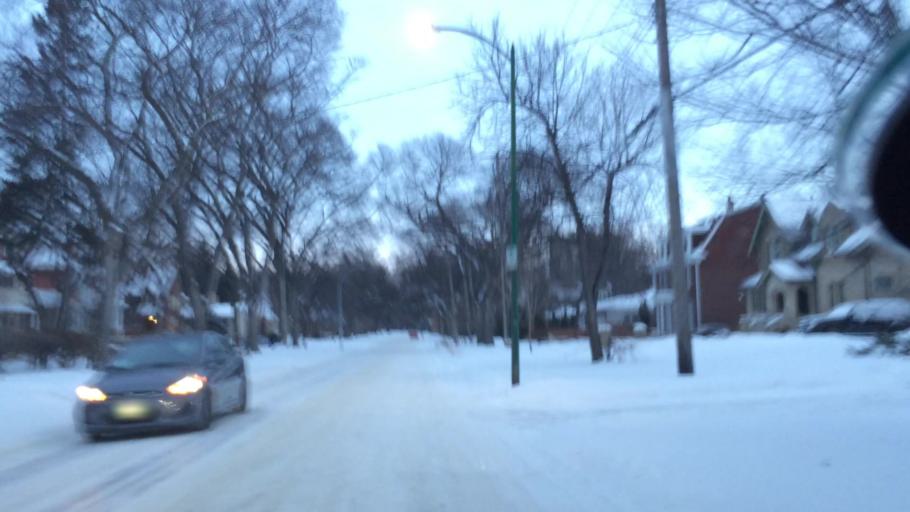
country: CA
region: Manitoba
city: Winnipeg
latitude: 49.8778
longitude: -97.1574
